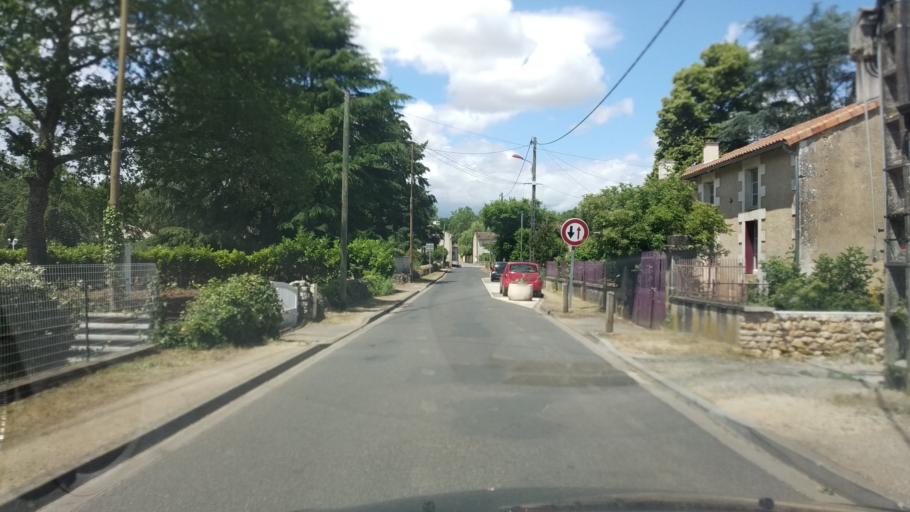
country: FR
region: Poitou-Charentes
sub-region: Departement de la Vienne
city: Cisse
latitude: 46.6048
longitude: 0.2393
